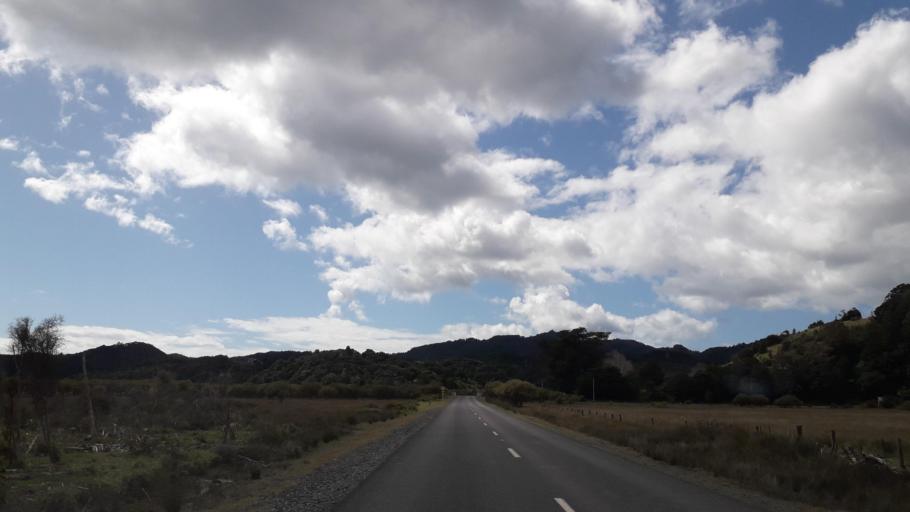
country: NZ
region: Northland
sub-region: Far North District
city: Paihia
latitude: -35.3379
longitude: 174.2286
